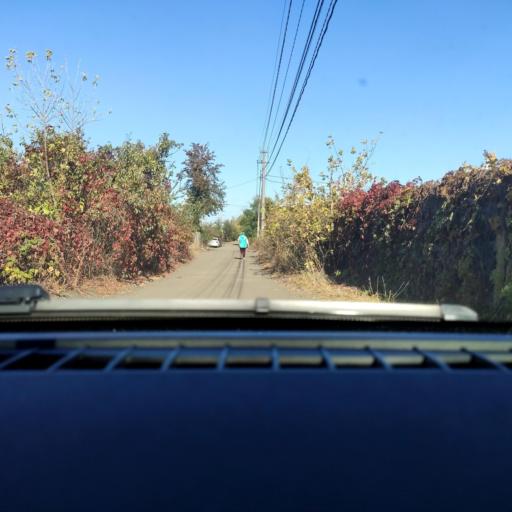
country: RU
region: Voronezj
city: Maslovka
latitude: 51.6045
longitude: 39.2782
